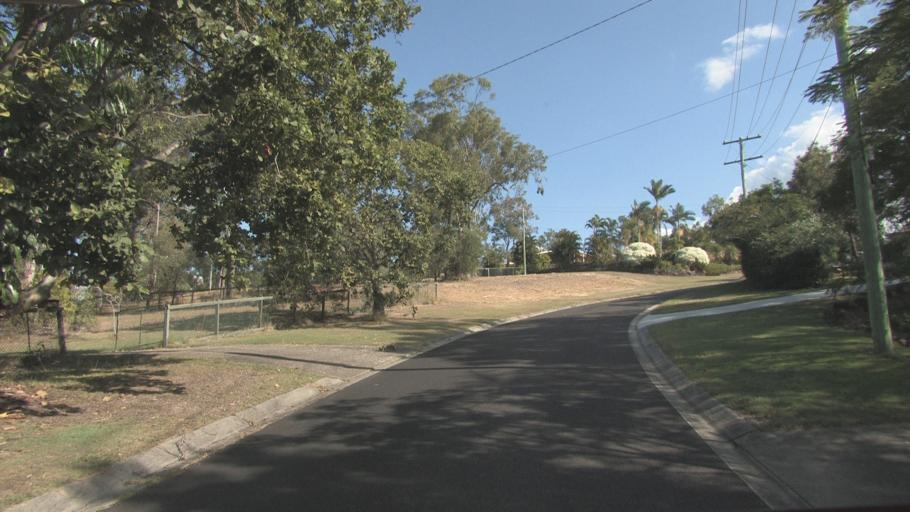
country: AU
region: Queensland
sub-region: Logan
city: Windaroo
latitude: -27.7351
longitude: 153.1917
